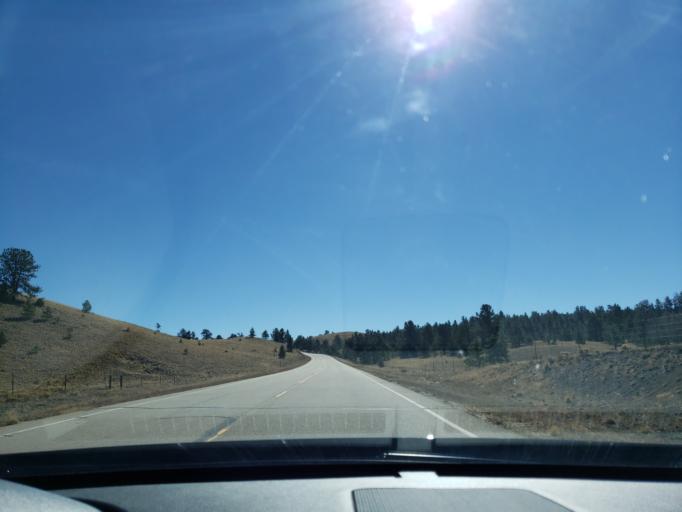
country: US
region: Colorado
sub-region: Chaffee County
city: Buena Vista
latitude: 38.8964
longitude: -105.6913
